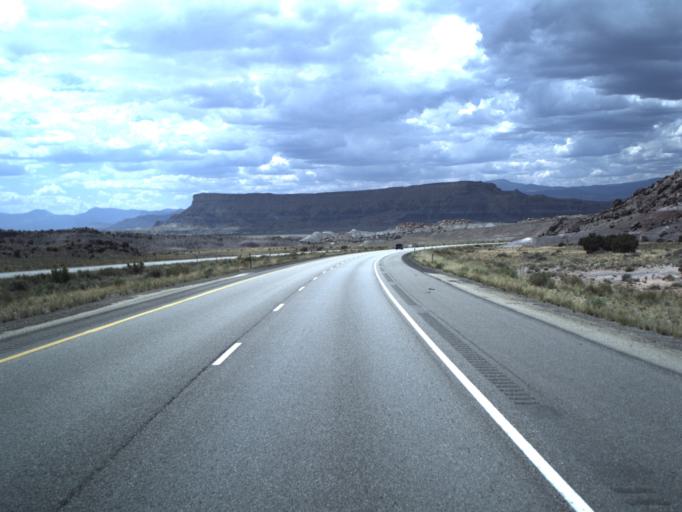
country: US
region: Utah
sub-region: Emery County
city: Ferron
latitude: 38.8211
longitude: -111.1522
